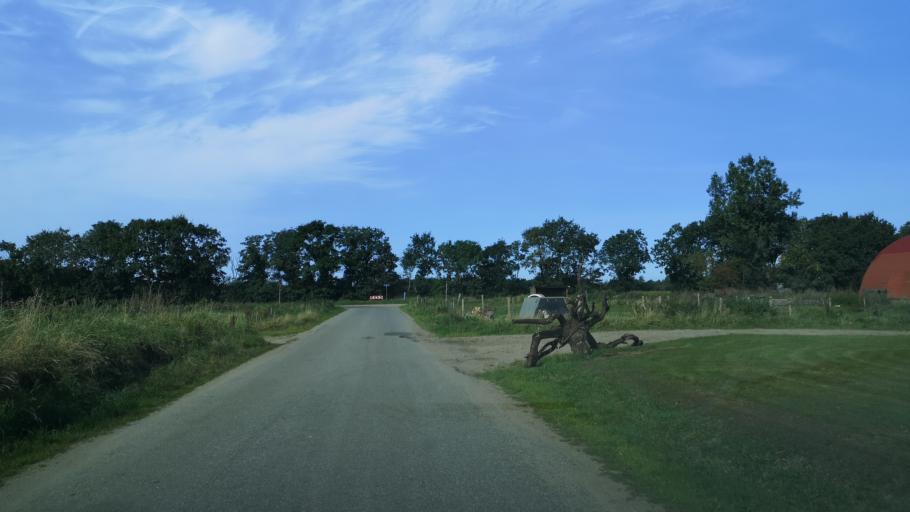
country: DK
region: Central Jutland
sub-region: Ikast-Brande Kommune
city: Ikast
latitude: 56.1568
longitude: 9.1207
